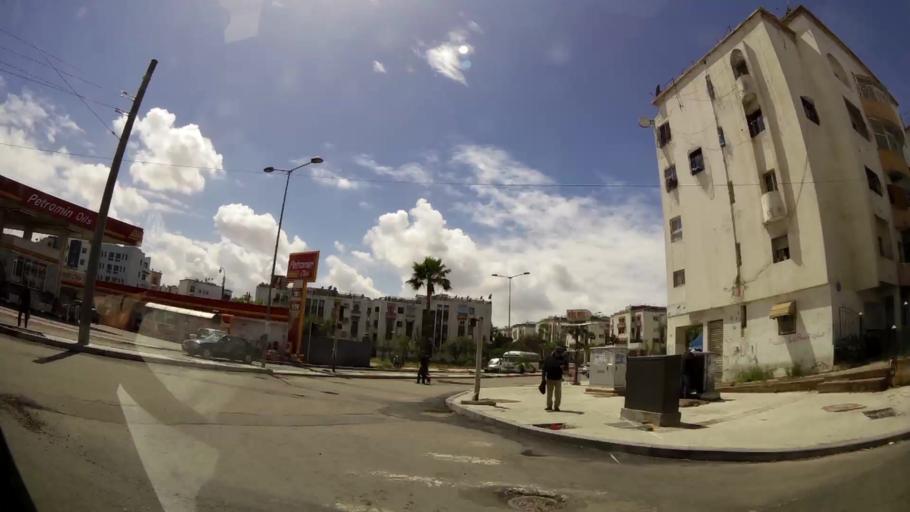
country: MA
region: Grand Casablanca
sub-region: Mediouna
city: Tit Mellil
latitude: 33.6066
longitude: -7.5191
